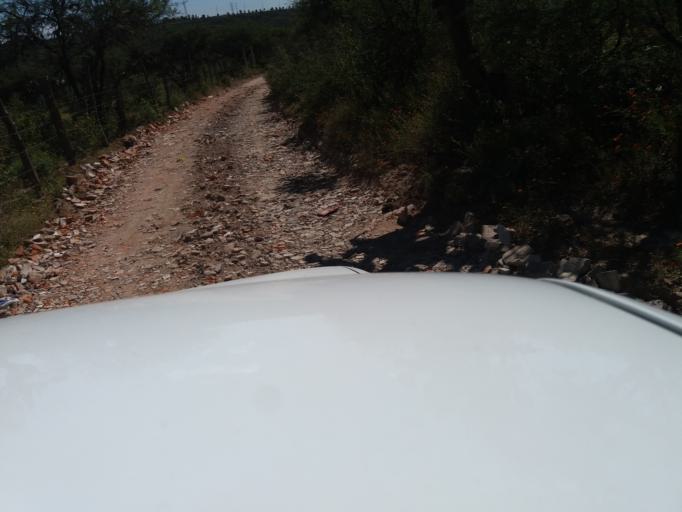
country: MX
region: Aguascalientes
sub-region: Aguascalientes
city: San Sebastian [Fraccionamiento]
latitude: 21.7760
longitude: -102.2294
